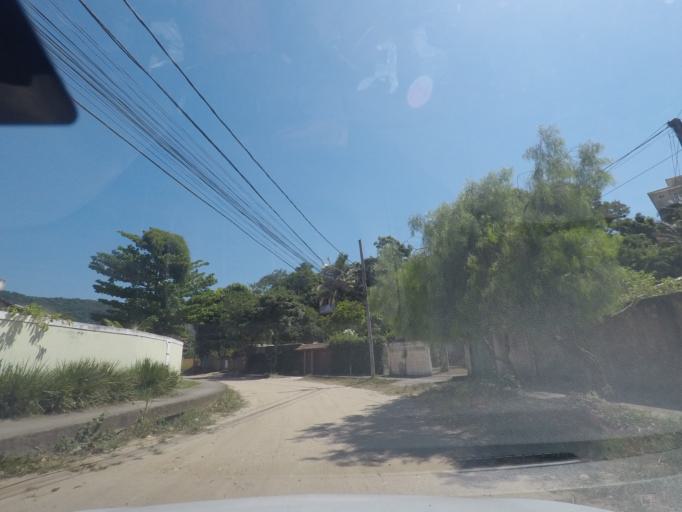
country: BR
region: Rio de Janeiro
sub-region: Niteroi
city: Niteroi
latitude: -22.9456
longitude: -43.0261
